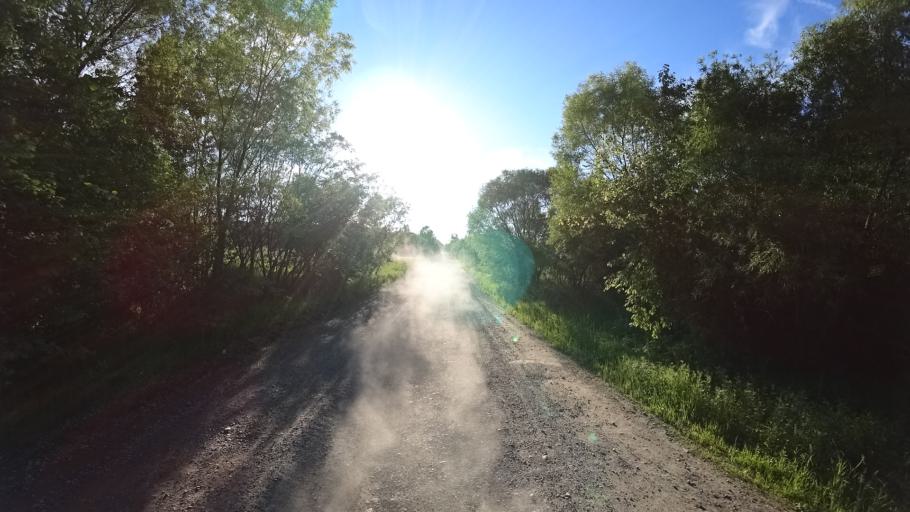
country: RU
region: Khabarovsk Krai
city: Khor
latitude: 47.8443
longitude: 134.9490
